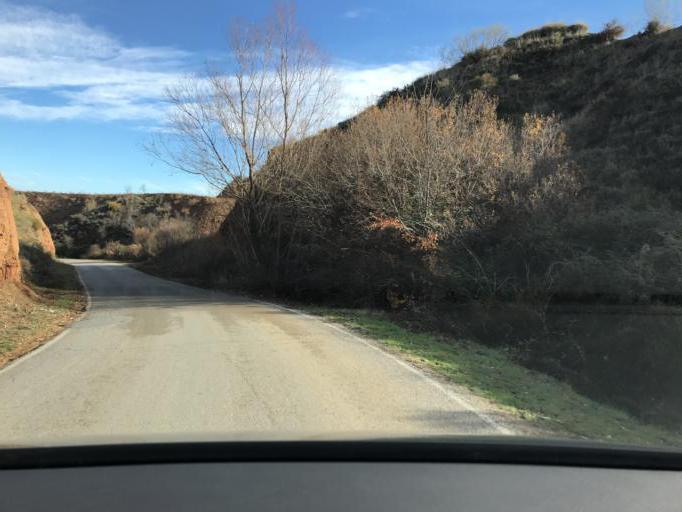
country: ES
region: Andalusia
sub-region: Provincia de Granada
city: Marchal
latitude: 37.2925
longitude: -3.2347
